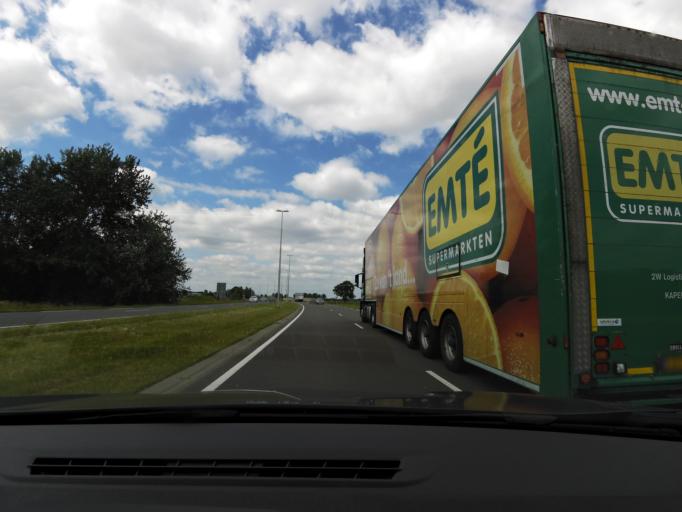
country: NL
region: North Brabant
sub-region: Gemeente Tilburg
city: Tilburg
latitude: 51.5888
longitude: 5.1096
